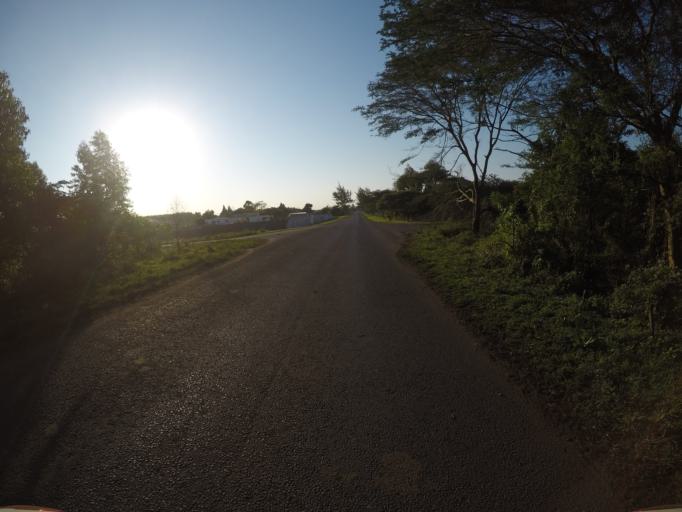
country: ZA
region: KwaZulu-Natal
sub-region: uThungulu District Municipality
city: KwaMbonambi
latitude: -28.6890
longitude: 32.2073
